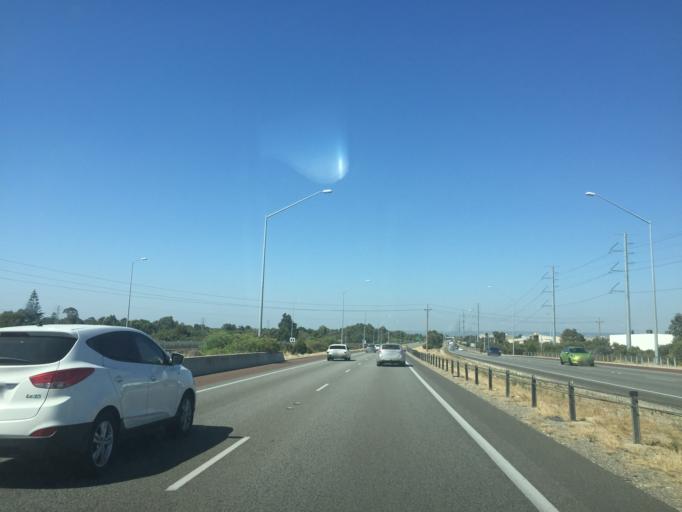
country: AU
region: Western Australia
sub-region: Canning
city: Willetton
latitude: -32.0680
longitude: 115.8912
